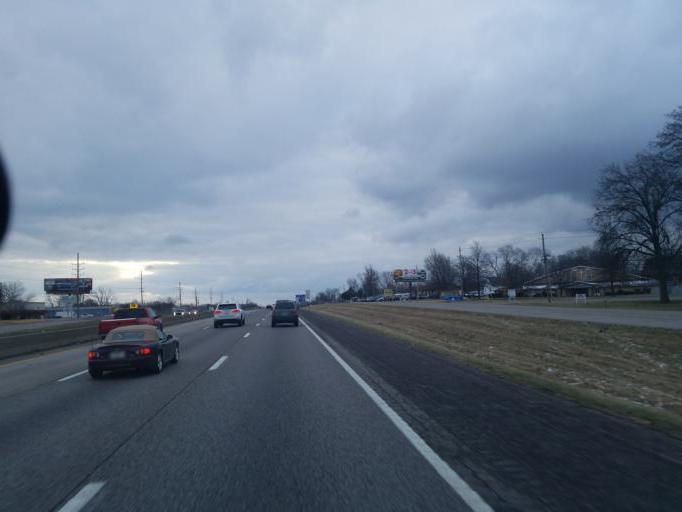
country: US
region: Missouri
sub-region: Saint Charles County
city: O'Fallon
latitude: 38.8025
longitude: -90.7263
